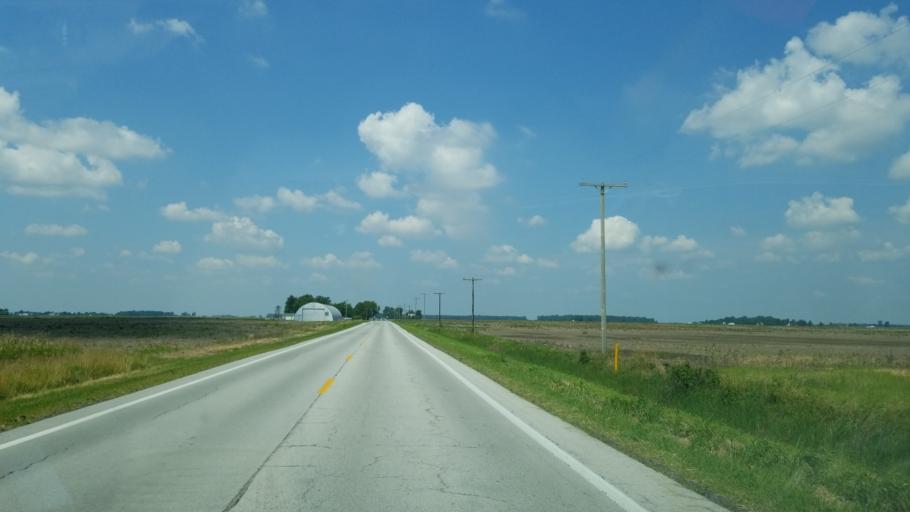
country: US
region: Ohio
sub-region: Wood County
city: Bowling Green
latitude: 41.2833
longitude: -83.6814
